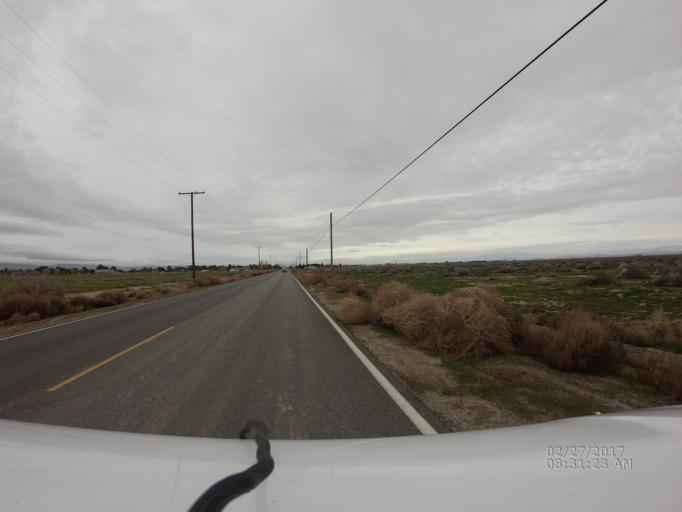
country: US
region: California
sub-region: Los Angeles County
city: Lancaster
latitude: 34.7046
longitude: -118.0462
